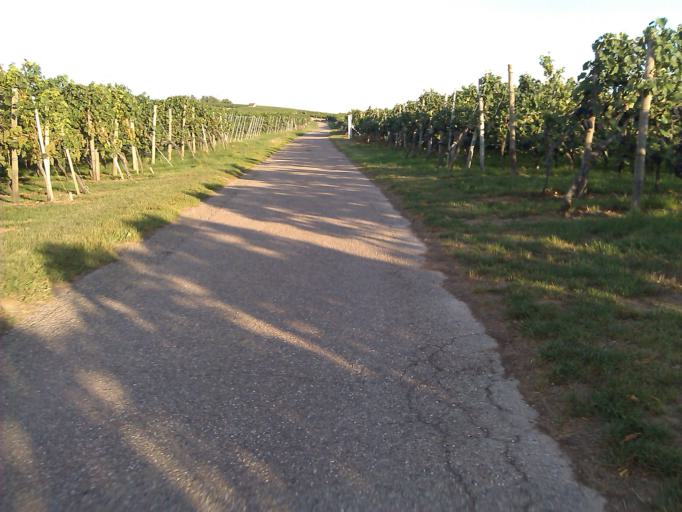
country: DE
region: Baden-Wuerttemberg
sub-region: Regierungsbezirk Stuttgart
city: Lauffen am Neckar
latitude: 49.0959
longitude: 9.1634
